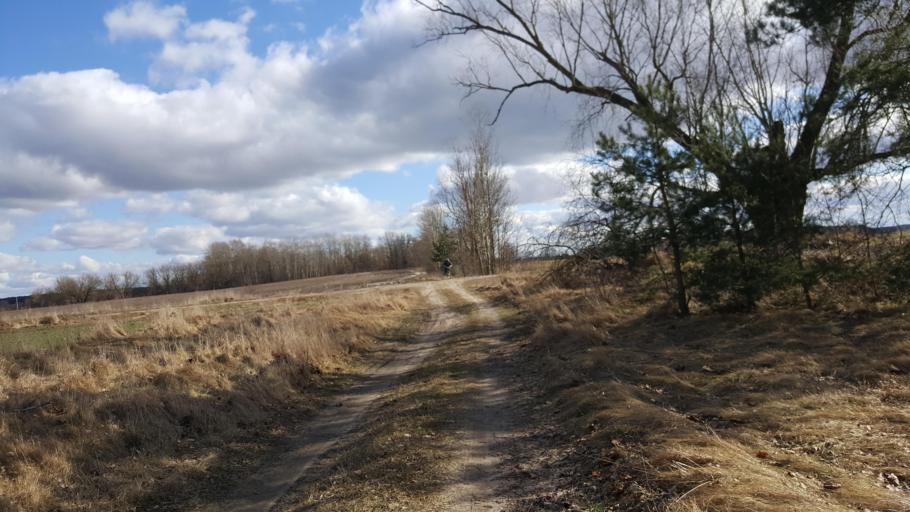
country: BY
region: Brest
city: Kamyanyets
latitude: 52.3910
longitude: 23.8788
